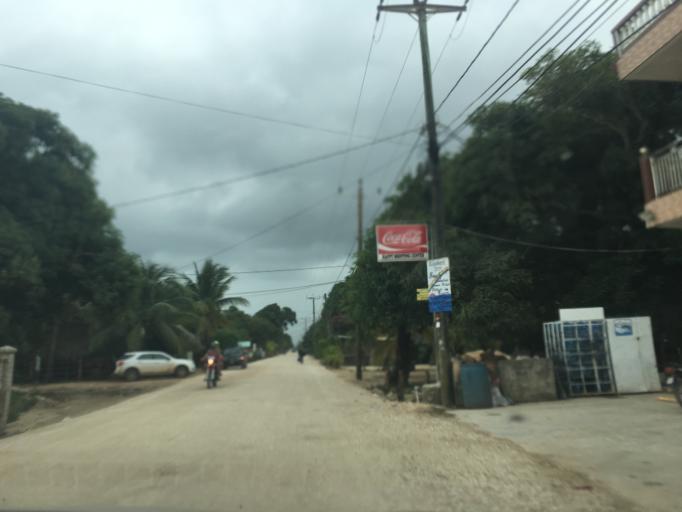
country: BZ
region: Stann Creek
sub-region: Dangriga
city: Dangriga
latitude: 16.8622
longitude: -88.2842
